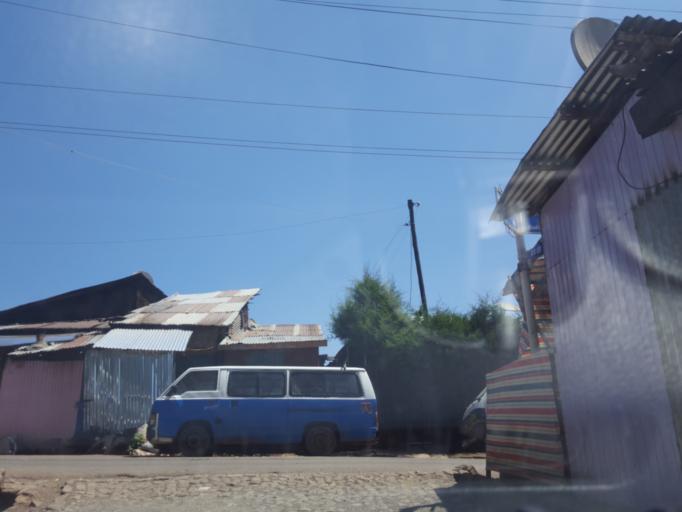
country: ET
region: Adis Abeba
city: Addis Ababa
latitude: 9.0628
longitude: 38.7481
